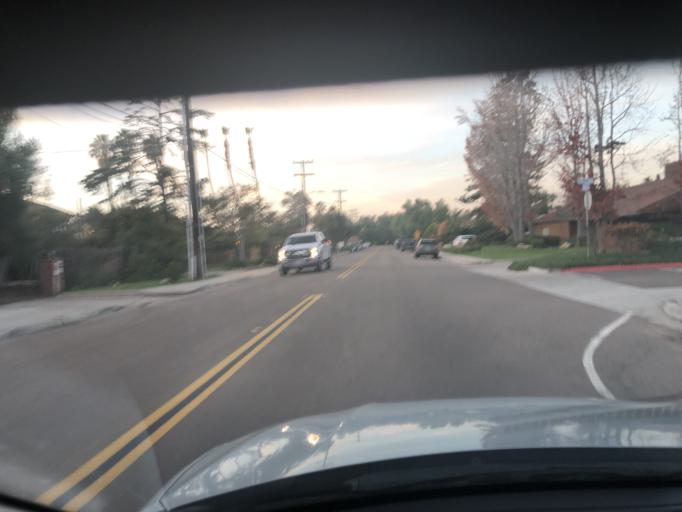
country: US
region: California
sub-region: San Diego County
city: Chula Vista
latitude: 32.6428
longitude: -117.0669
